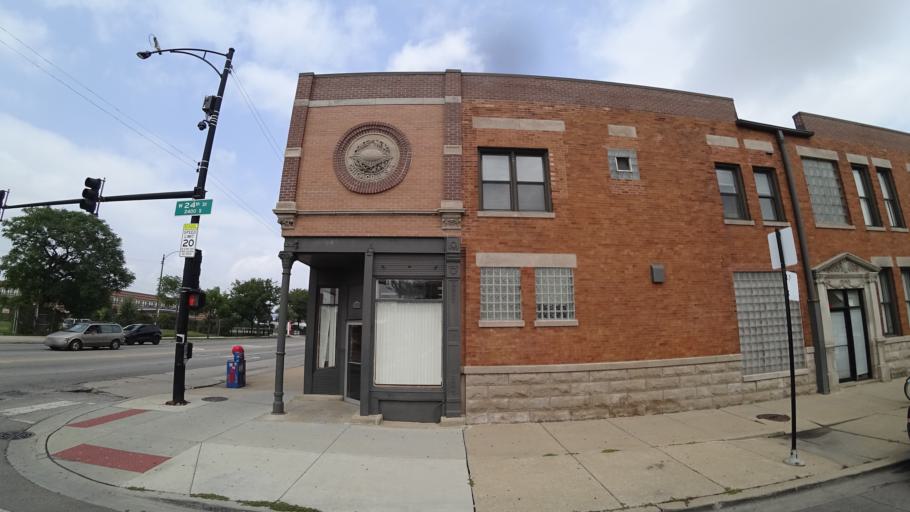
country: US
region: Illinois
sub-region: Cook County
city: Chicago
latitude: 41.8484
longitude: -87.6853
